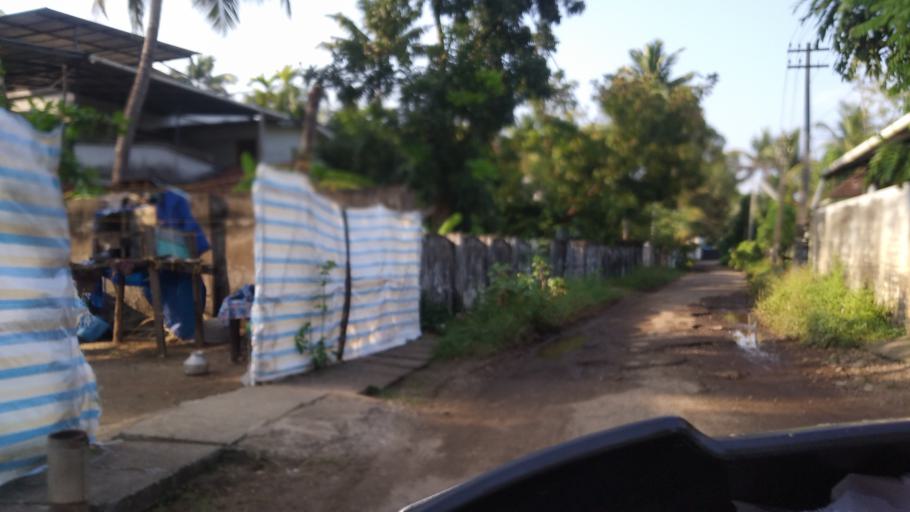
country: IN
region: Kerala
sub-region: Ernakulam
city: Elur
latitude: 10.0460
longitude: 76.2264
